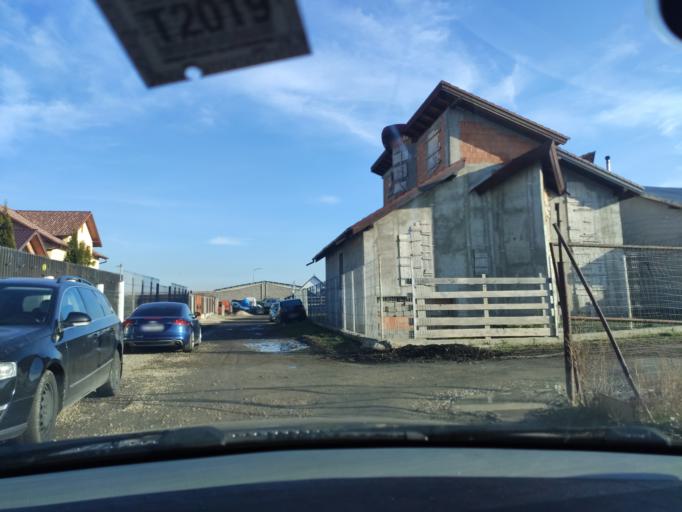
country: RO
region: Brasov
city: Codlea
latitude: 45.7062
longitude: 25.4547
